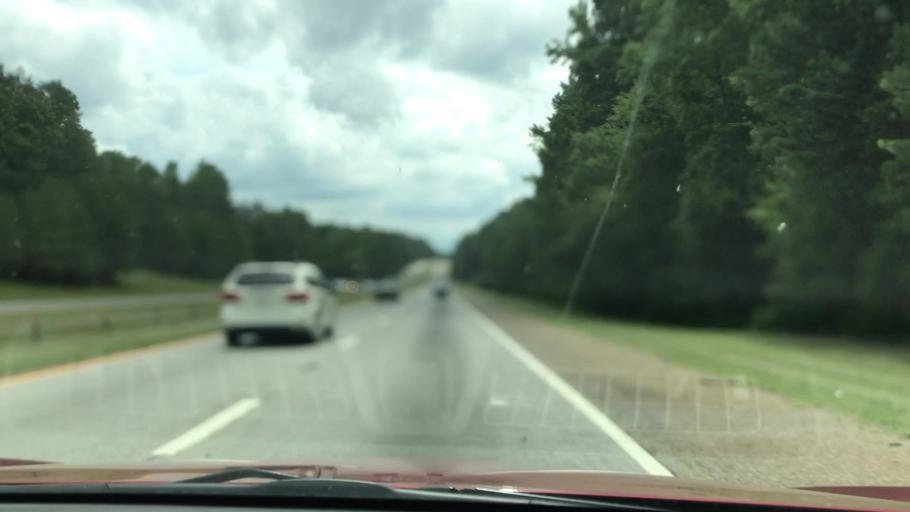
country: US
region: South Carolina
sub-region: Lexington County
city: Chapin
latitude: 34.1888
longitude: -81.3428
